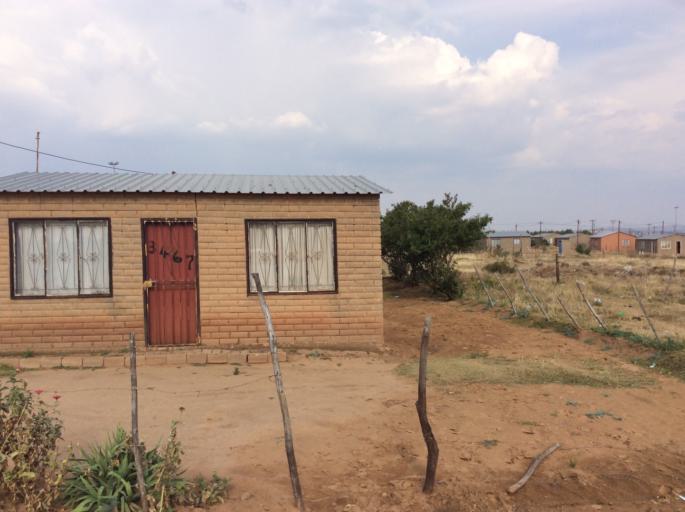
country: LS
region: Mafeteng
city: Mafeteng
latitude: -29.7095
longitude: 27.0145
